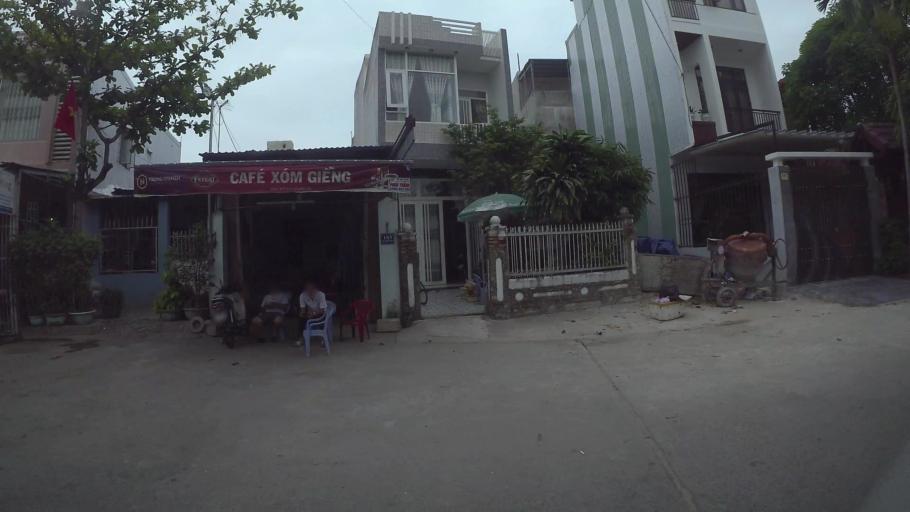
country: VN
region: Da Nang
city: Thanh Khe
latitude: 16.0687
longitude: 108.1778
